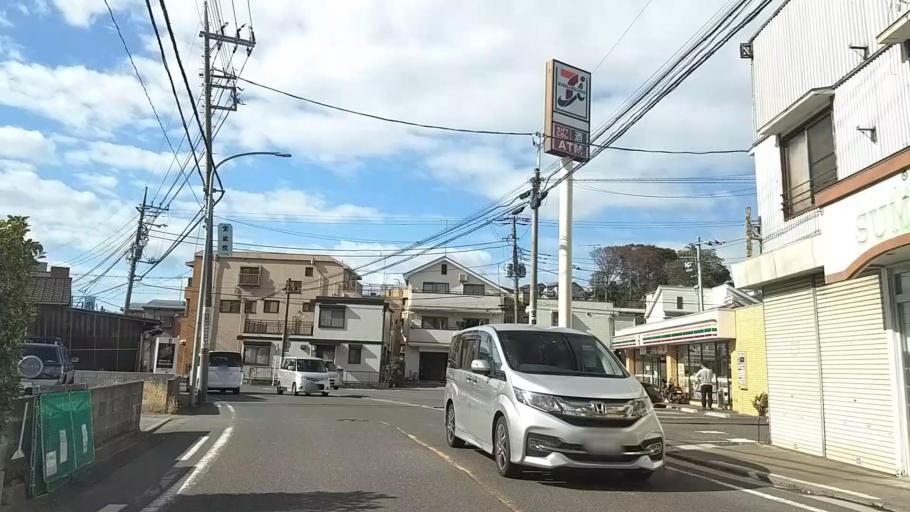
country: JP
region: Kanagawa
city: Yokohama
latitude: 35.5056
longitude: 139.6561
